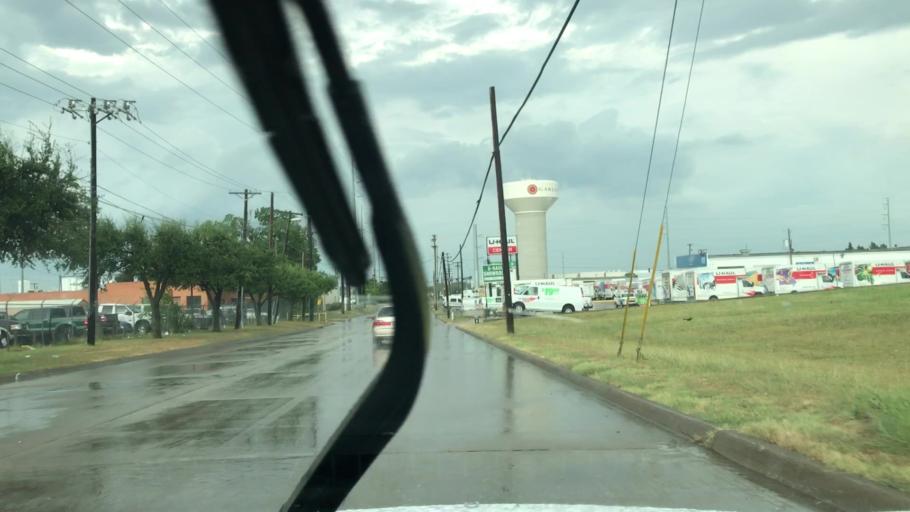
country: US
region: Texas
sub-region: Dallas County
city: Garland
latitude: 32.8715
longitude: -96.6679
